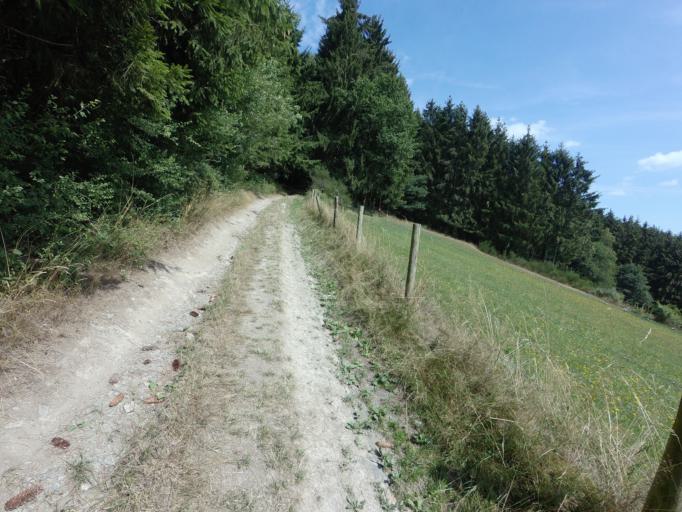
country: DE
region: North Rhine-Westphalia
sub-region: Regierungsbezirk Koln
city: Simmerath
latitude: 50.5989
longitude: 6.3803
